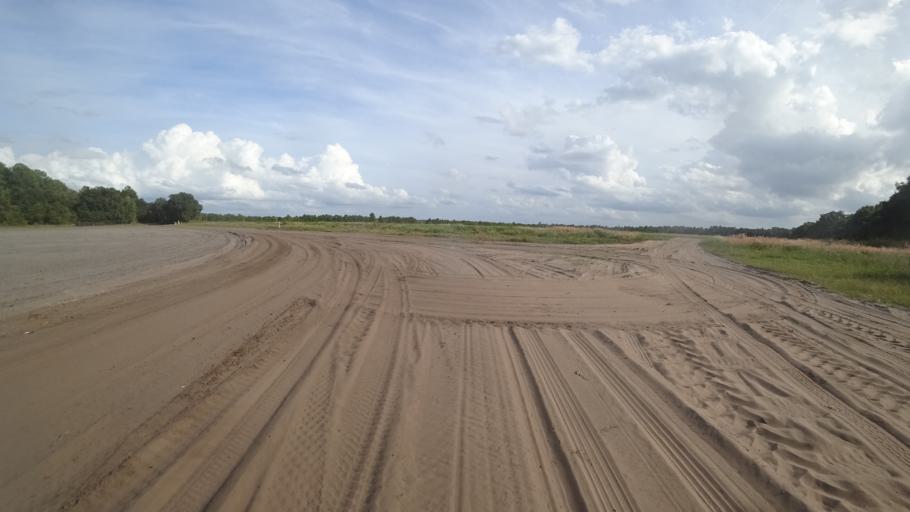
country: US
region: Florida
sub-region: Hillsborough County
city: Wimauma
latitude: 27.5962
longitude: -82.1418
